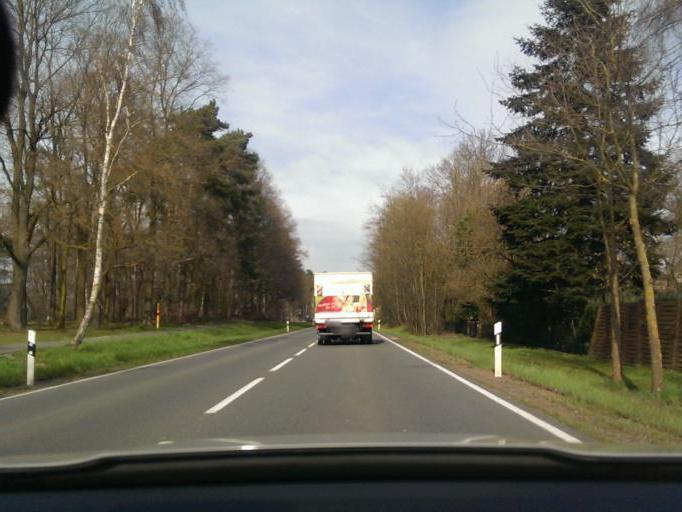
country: DE
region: North Rhine-Westphalia
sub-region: Regierungsbezirk Detmold
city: Hovelhof
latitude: 51.7850
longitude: 8.6127
